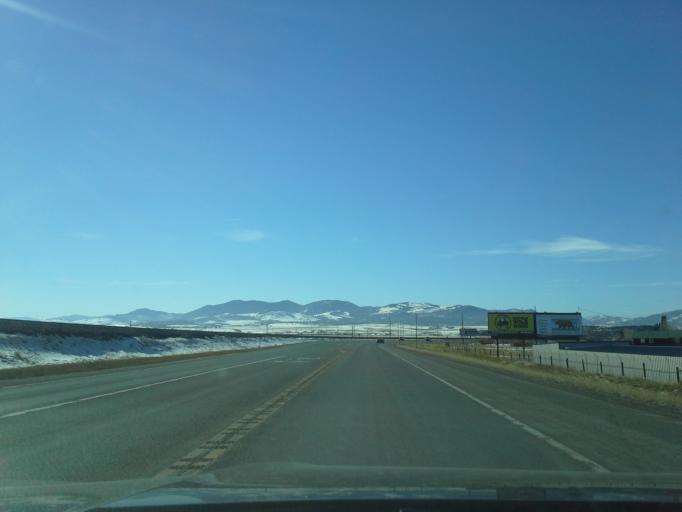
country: US
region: Montana
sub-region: Lewis and Clark County
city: East Helena
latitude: 46.5866
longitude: -111.8942
